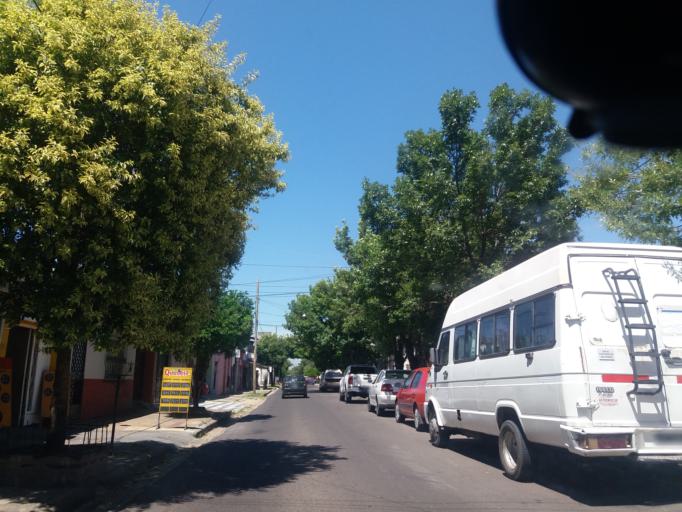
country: AR
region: Corrientes
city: Corrientes
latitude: -27.4787
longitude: -58.8448
